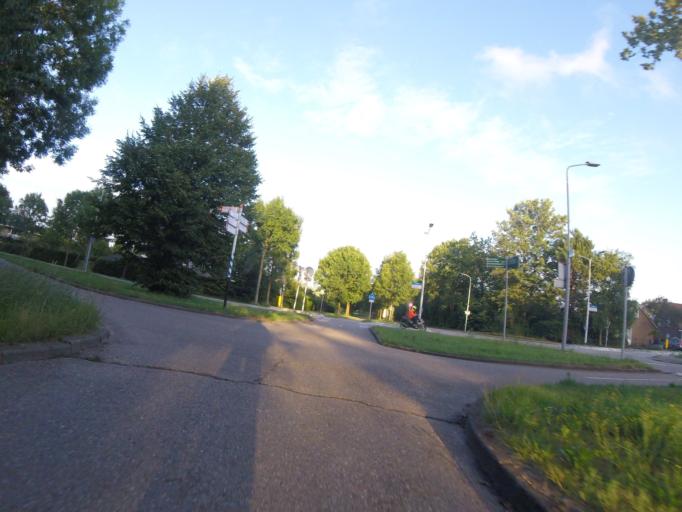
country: NL
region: North Holland
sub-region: Gemeente Haarlemmermeer
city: Hoofddorp
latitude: 52.3195
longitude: 4.6723
